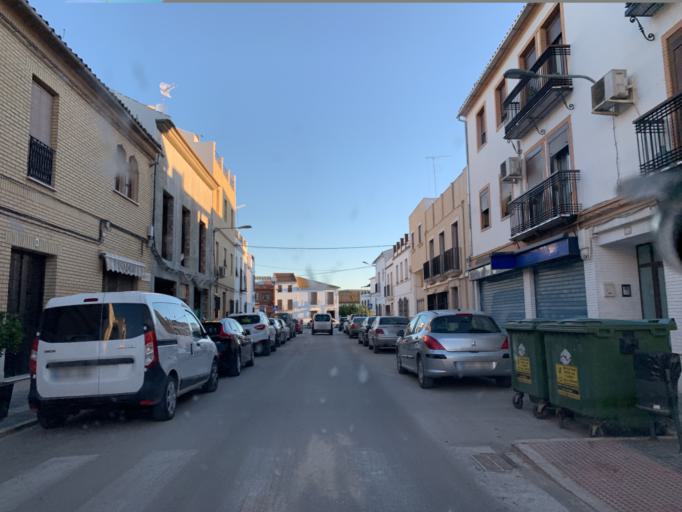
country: ES
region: Andalusia
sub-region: Provincia de Sevilla
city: Pedrera
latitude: 37.2236
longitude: -4.8935
